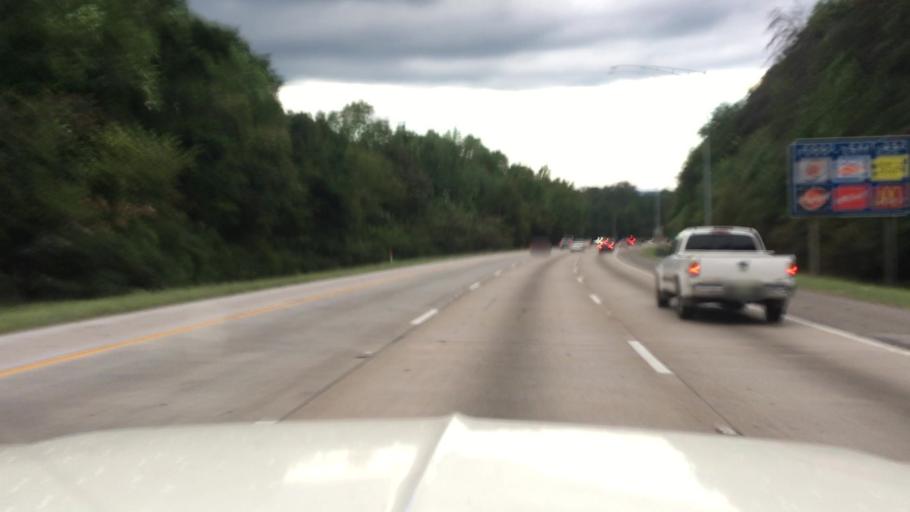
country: US
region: Alabama
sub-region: Jefferson County
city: Hoover
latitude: 33.4242
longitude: -86.8164
